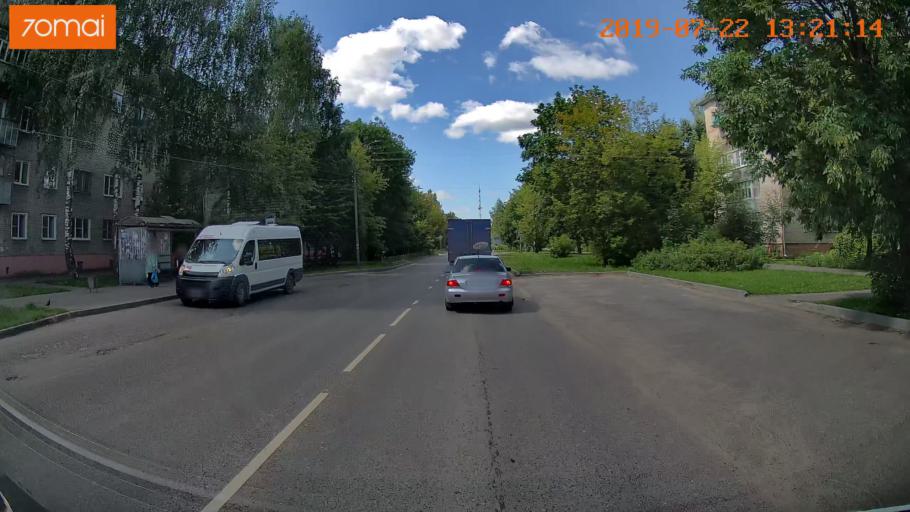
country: RU
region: Ivanovo
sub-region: Gorod Ivanovo
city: Ivanovo
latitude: 57.0220
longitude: 40.9644
